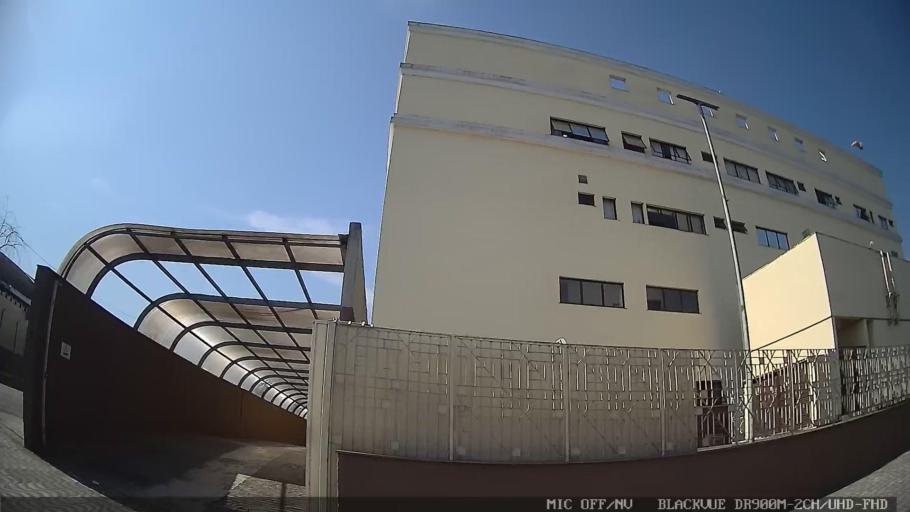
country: BR
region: Sao Paulo
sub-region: Guaruja
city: Guaruja
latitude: -23.9845
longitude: -46.2683
